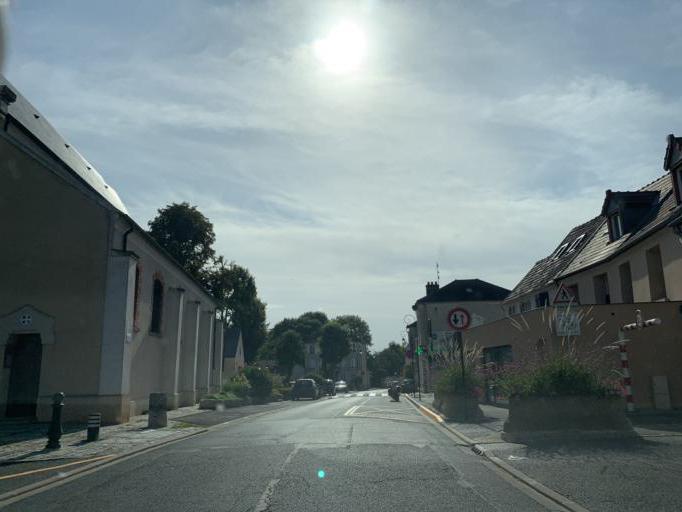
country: FR
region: Ile-de-France
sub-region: Departement de Seine-et-Marne
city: Annet-sur-Marne
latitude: 48.9259
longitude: 2.7203
